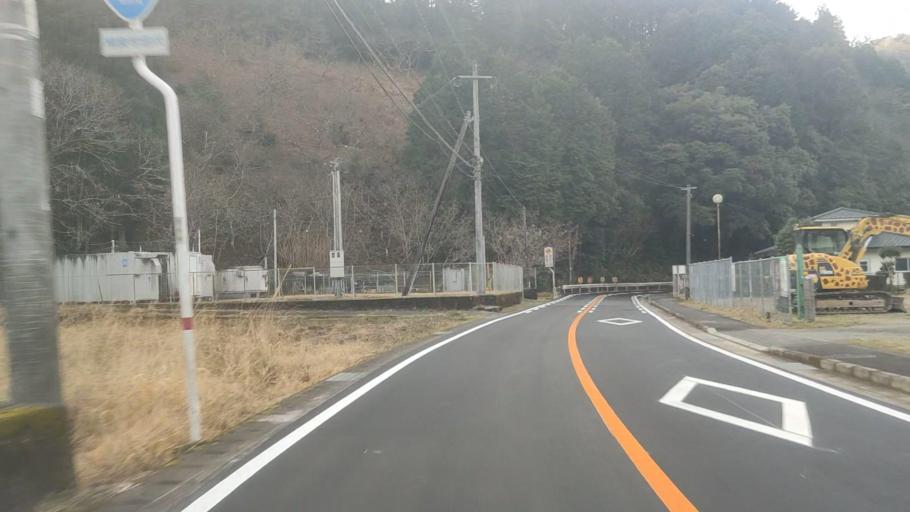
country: JP
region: Kumamoto
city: Hitoyoshi
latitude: 32.3037
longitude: 130.8470
